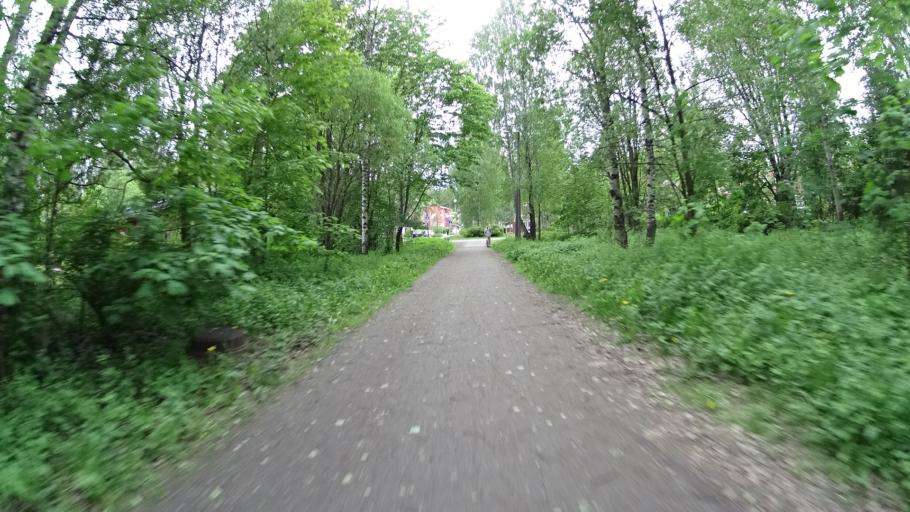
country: FI
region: Uusimaa
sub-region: Helsinki
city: Vantaa
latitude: 60.2199
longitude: 25.0507
